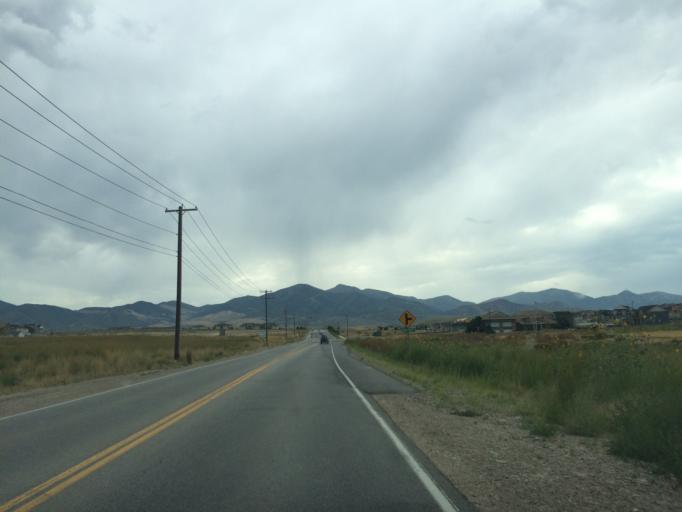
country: US
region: Utah
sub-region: Salt Lake County
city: Oquirrh
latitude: 40.6094
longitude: -112.0409
